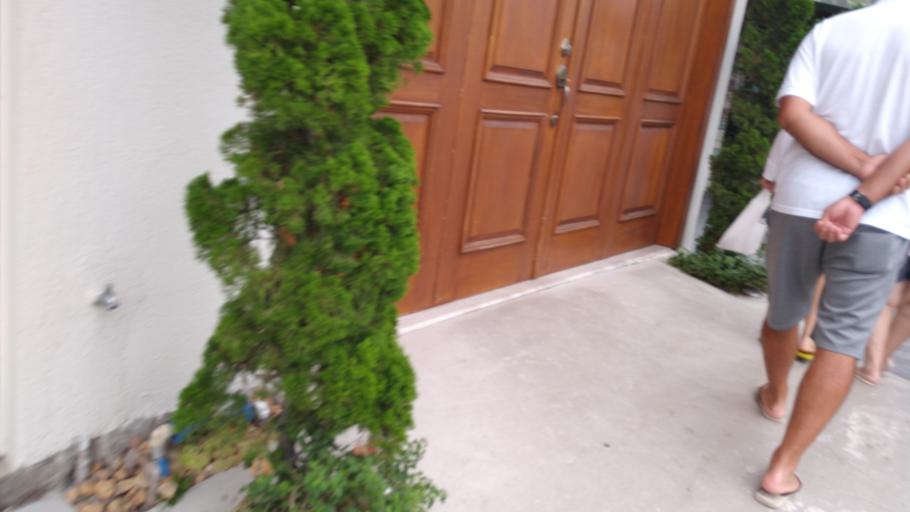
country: BR
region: Santa Catarina
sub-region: Itapema
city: Itapema
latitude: -27.0962
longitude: -48.6164
